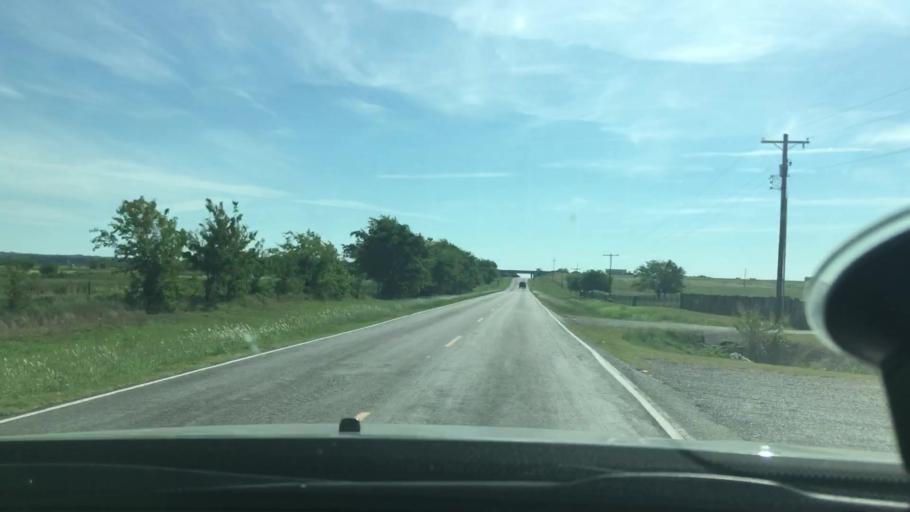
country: US
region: Oklahoma
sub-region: Carter County
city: Ardmore
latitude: 34.3327
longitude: -97.1608
